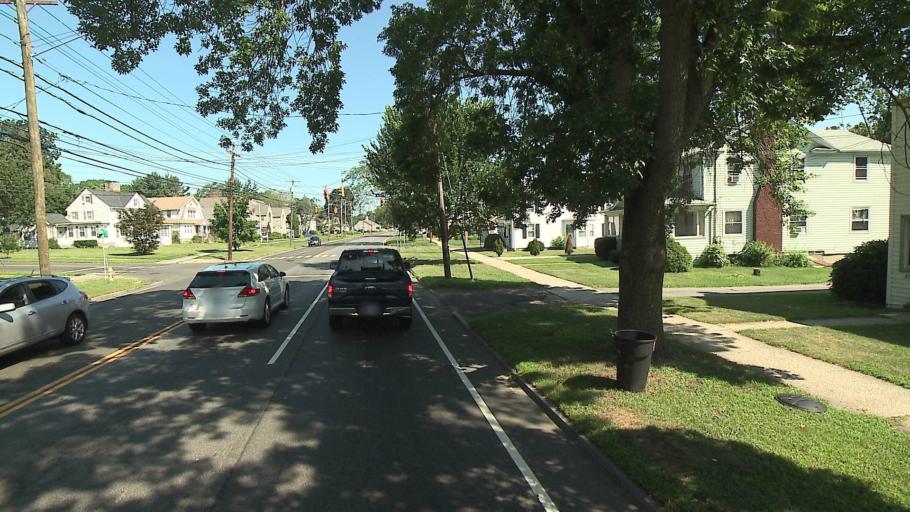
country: US
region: Connecticut
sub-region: Fairfield County
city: Stratford
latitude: 41.2037
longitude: -73.1315
